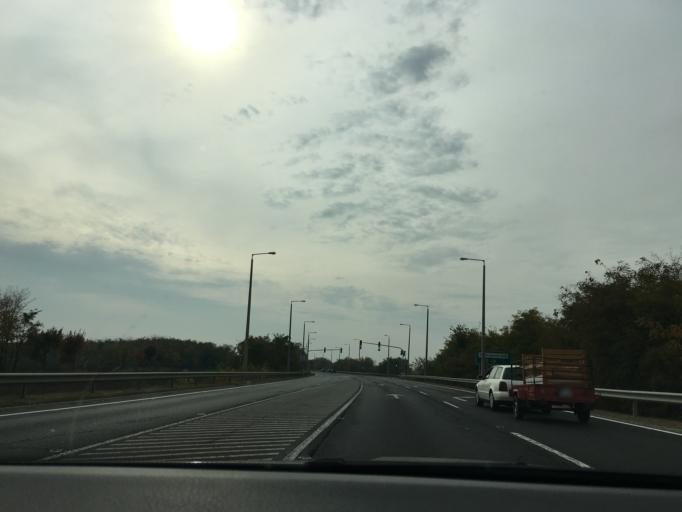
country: HU
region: Hajdu-Bihar
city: Hajduszoboszlo
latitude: 47.4608
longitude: 21.4482
